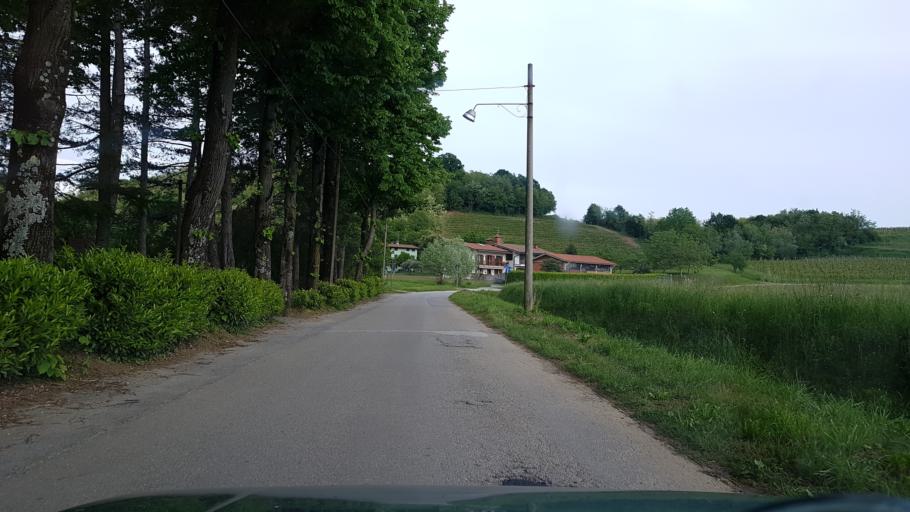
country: IT
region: Friuli Venezia Giulia
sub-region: Provincia di Gorizia
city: Cormons
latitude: 45.9565
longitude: 13.4844
